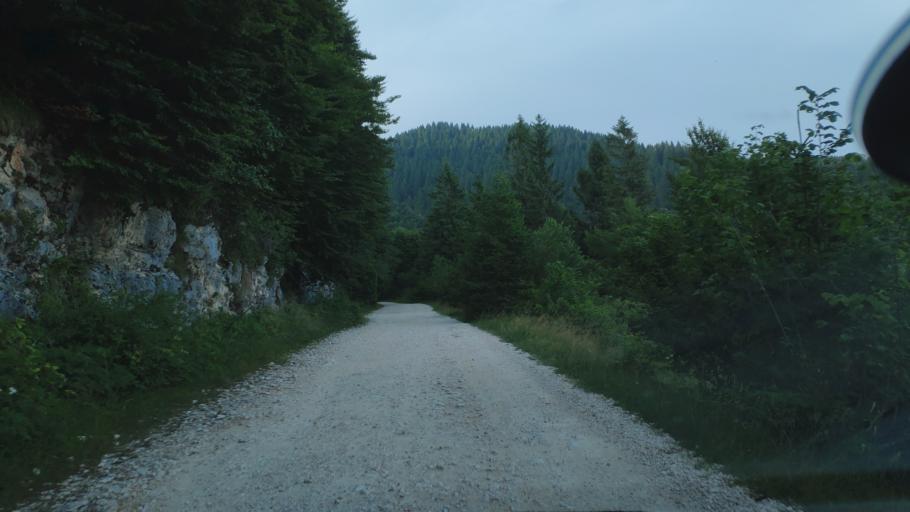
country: IT
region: Veneto
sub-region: Provincia di Vicenza
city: Calvene
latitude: 45.7994
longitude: 11.5003
